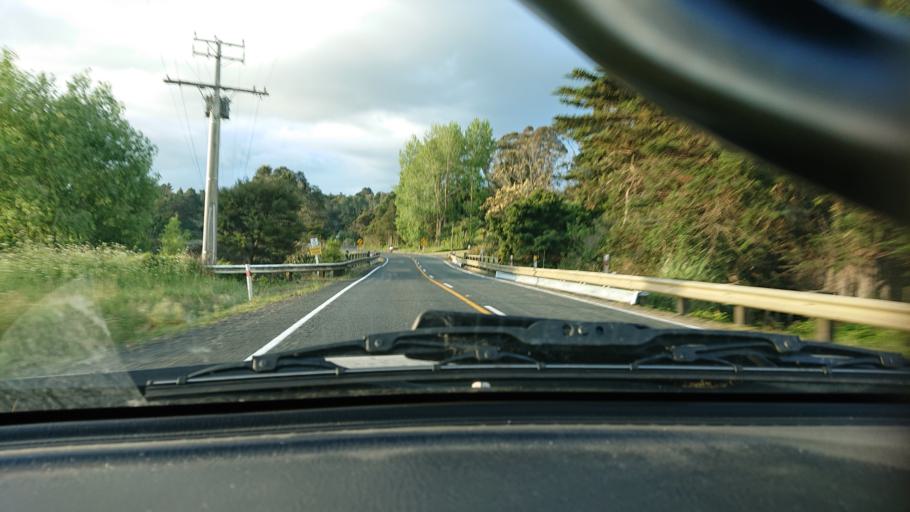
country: NZ
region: Auckland
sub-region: Auckland
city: Parakai
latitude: -36.5321
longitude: 174.4557
